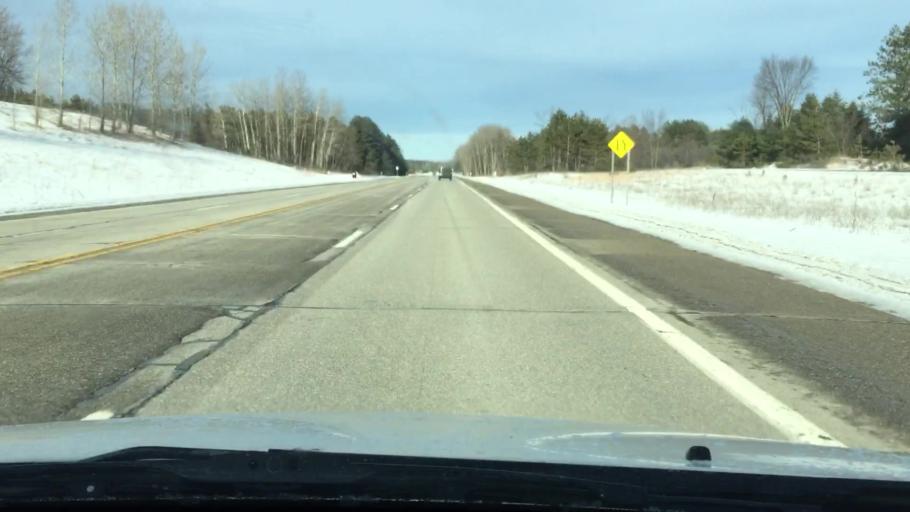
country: US
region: Michigan
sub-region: Kalkaska County
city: Kalkaska
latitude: 44.6213
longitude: -85.2994
